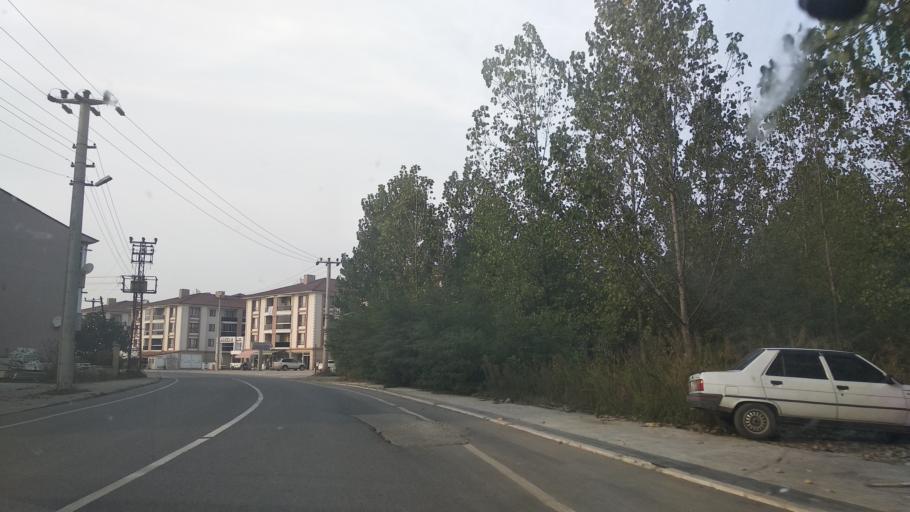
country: TR
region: Duzce
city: Duzce
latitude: 40.8296
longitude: 31.1719
